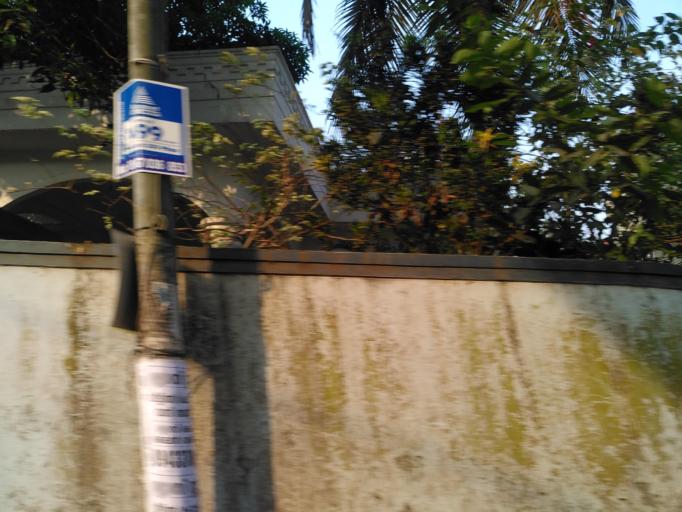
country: IN
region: Kerala
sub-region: Ernakulam
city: Cochin
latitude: 9.9368
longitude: 76.3236
